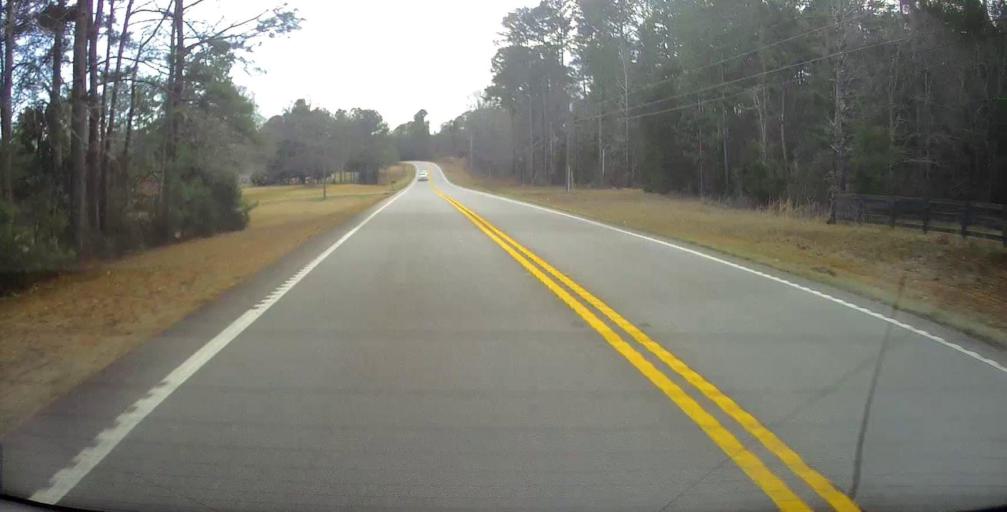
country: US
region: Georgia
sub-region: Troup County
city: West Point
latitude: 32.9319
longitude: -85.1547
